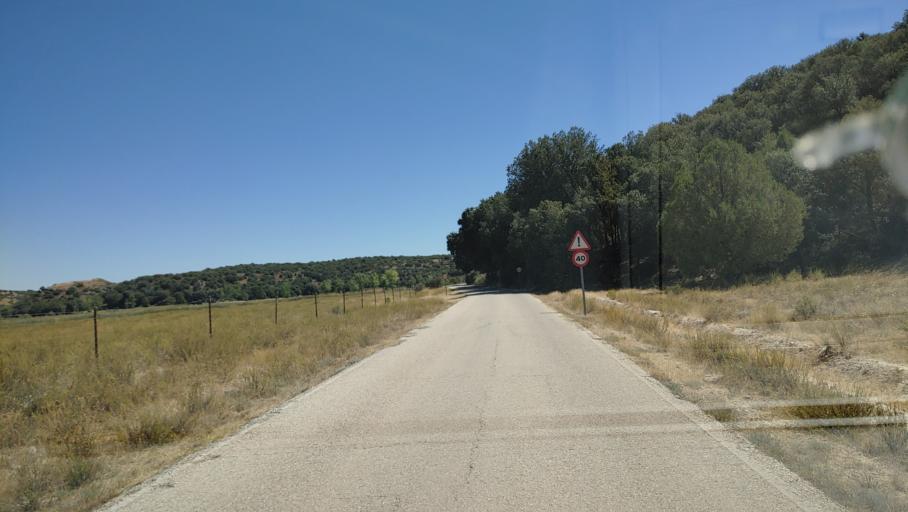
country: ES
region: Castille-La Mancha
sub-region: Provincia de Ciudad Real
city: Ruidera
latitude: 38.9256
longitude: -2.8281
